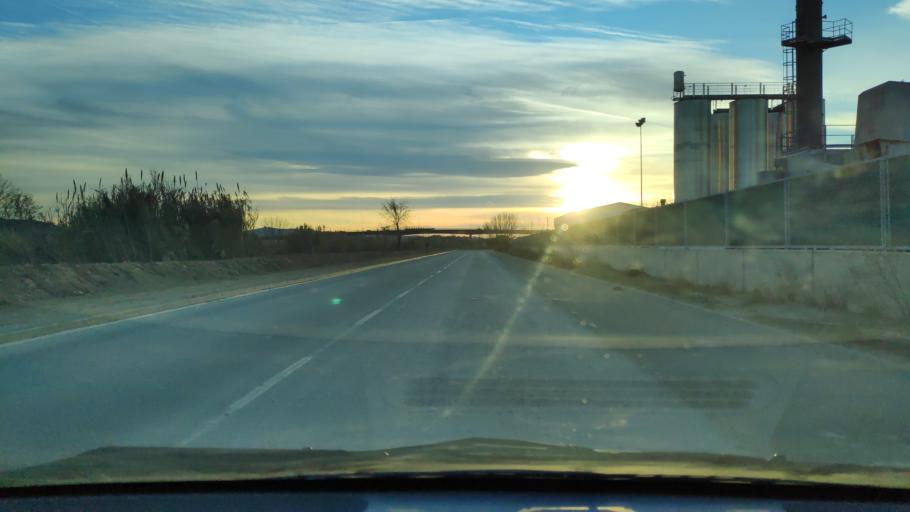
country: ES
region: Catalonia
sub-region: Provincia de Barcelona
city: Montmelo
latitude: 41.5432
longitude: 2.2330
